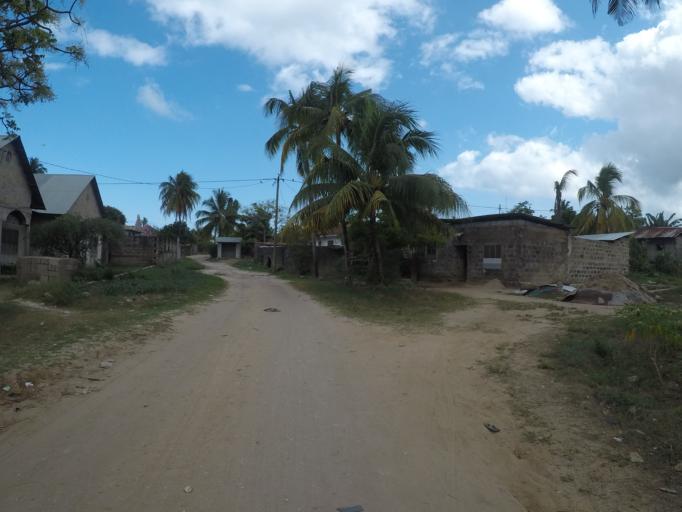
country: TZ
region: Zanzibar Urban/West
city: Zanzibar
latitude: -6.1866
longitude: 39.2148
